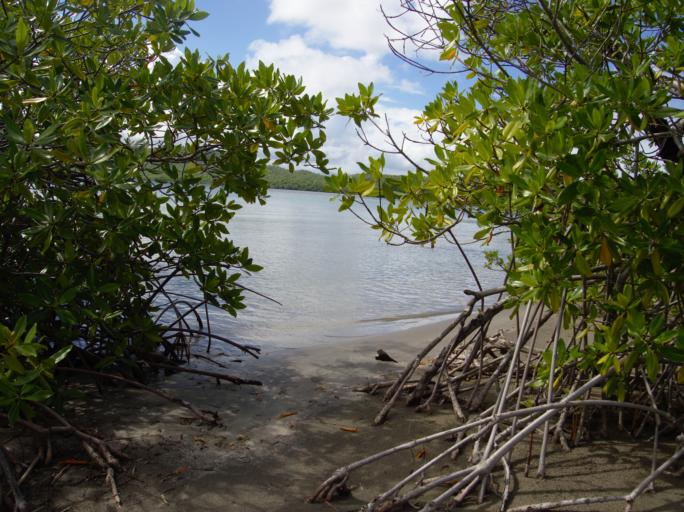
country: MQ
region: Martinique
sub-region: Martinique
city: La Trinite
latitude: 14.7653
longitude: -60.8822
